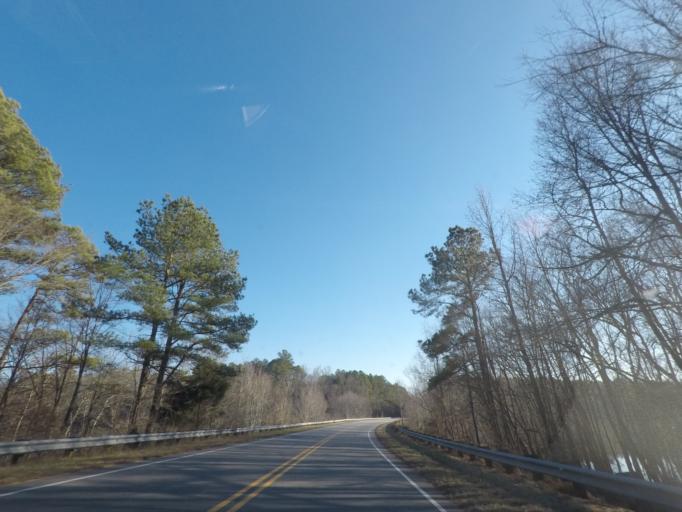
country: US
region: North Carolina
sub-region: Granville County
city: Butner
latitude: 36.0821
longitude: -78.7558
